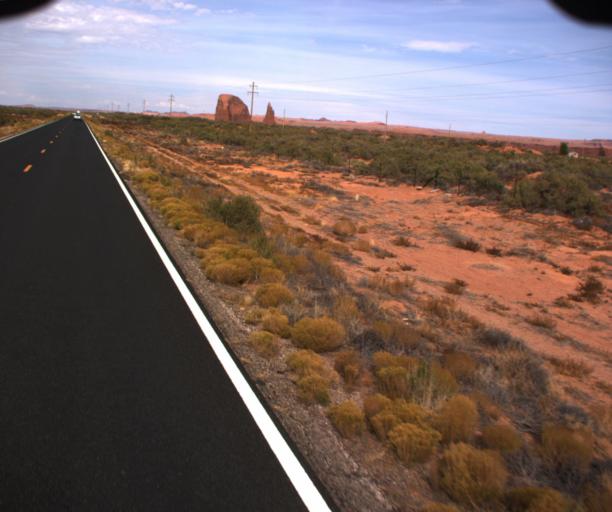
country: US
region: Arizona
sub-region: Apache County
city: Many Farms
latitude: 36.6325
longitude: -109.5857
